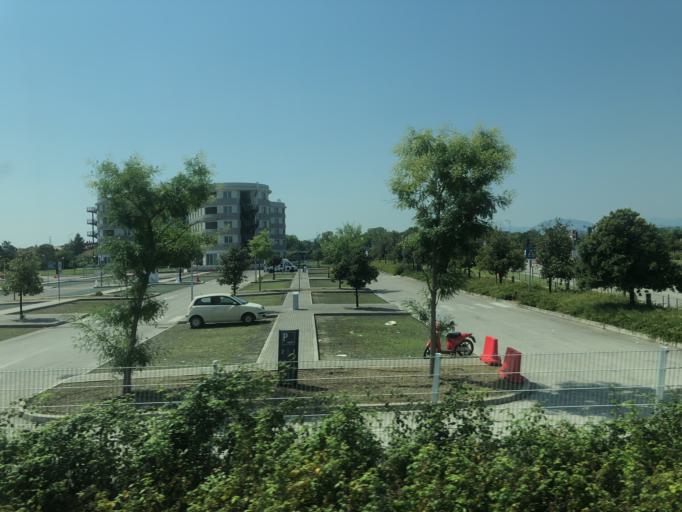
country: IT
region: Emilia-Romagna
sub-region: Provincia di Rimini
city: Rimini
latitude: 44.0707
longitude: 12.5276
